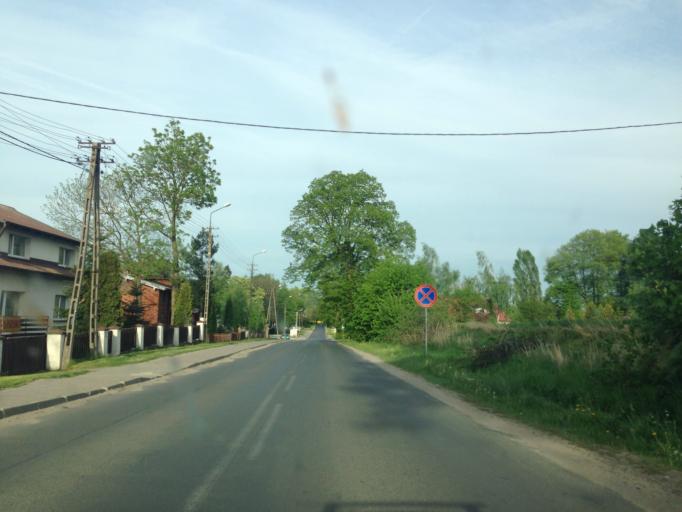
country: PL
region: Kujawsko-Pomorskie
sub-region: Powiat wabrzeski
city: Pluznica
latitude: 53.2918
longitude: 18.7784
